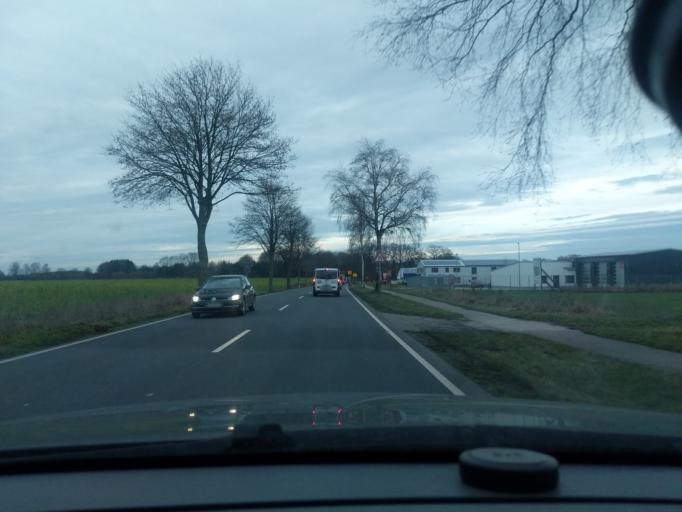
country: DE
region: Lower Saxony
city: Sauensiek
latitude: 53.3747
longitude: 9.5946
